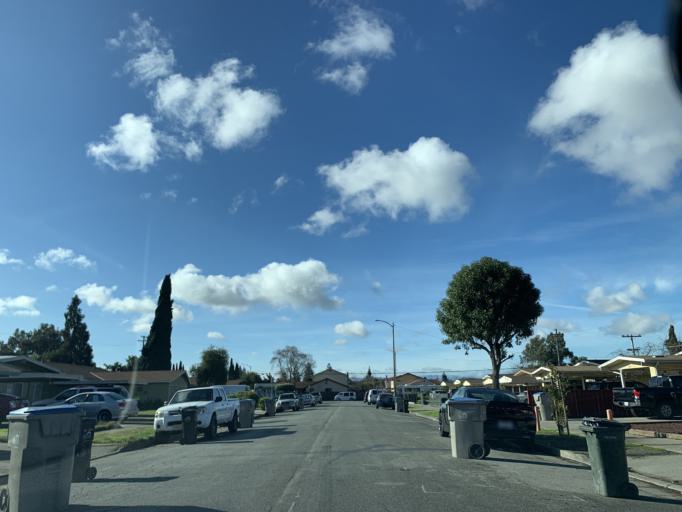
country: US
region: California
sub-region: Santa Clara County
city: Alum Rock
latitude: 37.3466
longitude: -121.8350
